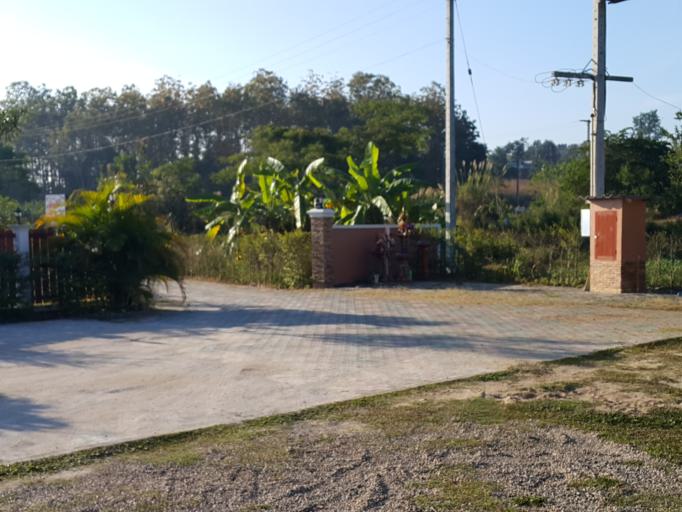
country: TH
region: Chiang Mai
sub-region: Amphoe Chiang Dao
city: Chiang Dao
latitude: 19.3883
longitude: 98.9530
